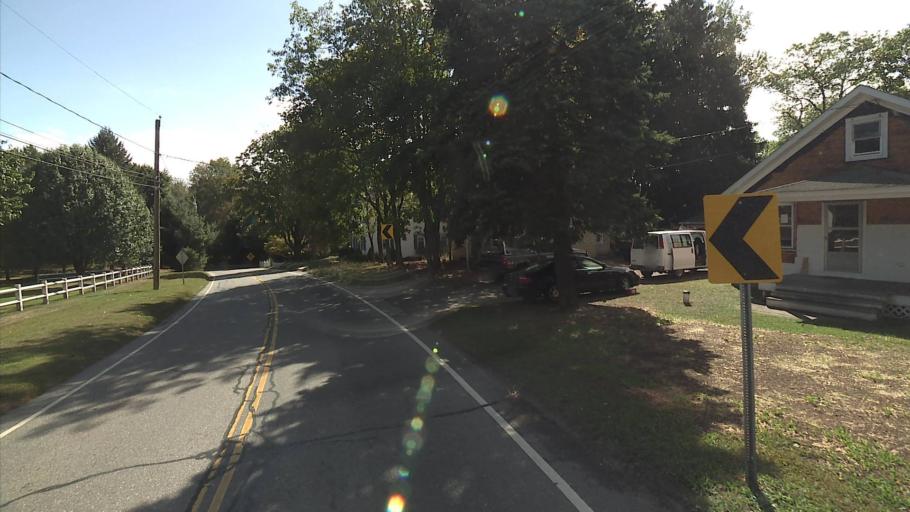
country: US
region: Connecticut
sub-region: Middlesex County
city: Durham
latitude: 41.5133
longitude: -72.7278
